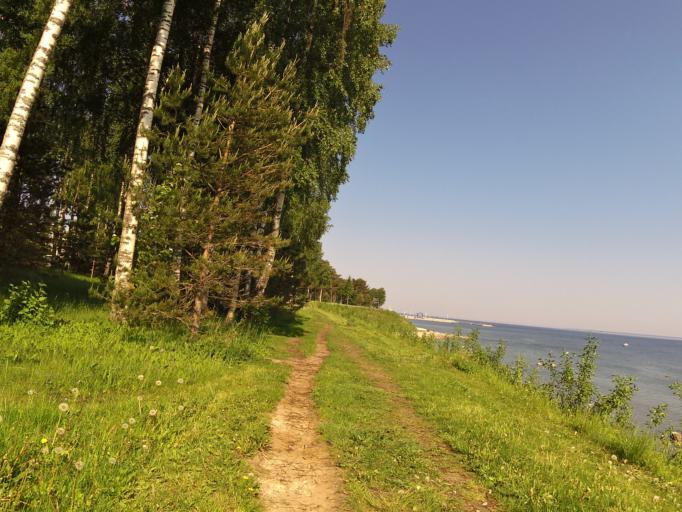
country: EE
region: Harju
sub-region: Harku vald
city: Tabasalu
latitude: 59.4450
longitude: 24.6187
